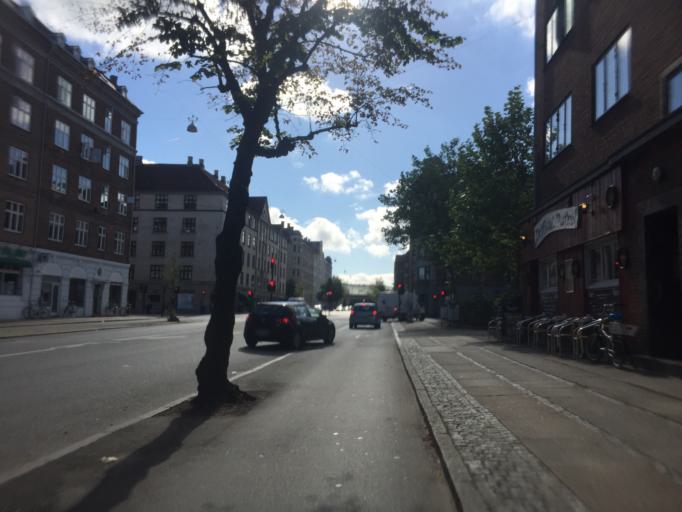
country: DK
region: Capital Region
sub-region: Frederiksberg Kommune
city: Frederiksberg
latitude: 55.6939
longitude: 12.5320
